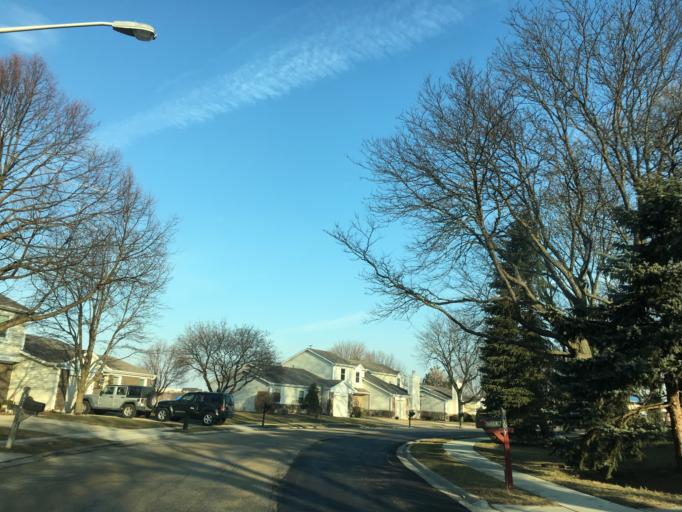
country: US
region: Illinois
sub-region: Cook County
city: Schaumburg
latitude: 42.0459
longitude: -88.1029
